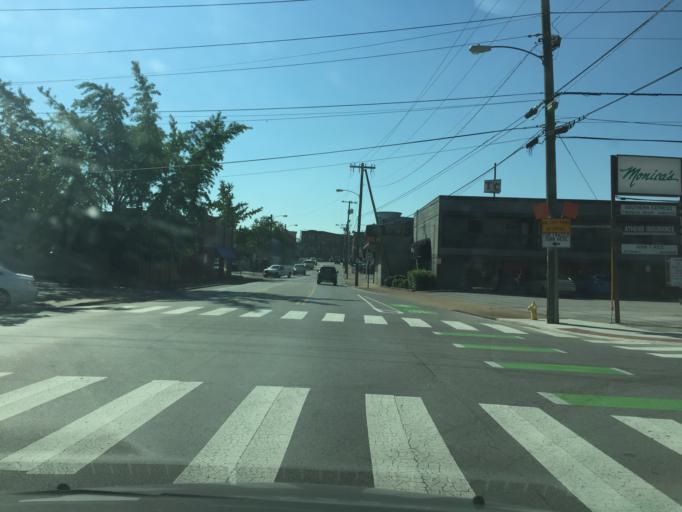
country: US
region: Tennessee
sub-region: Hamilton County
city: Chattanooga
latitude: 35.0647
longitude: -85.3090
